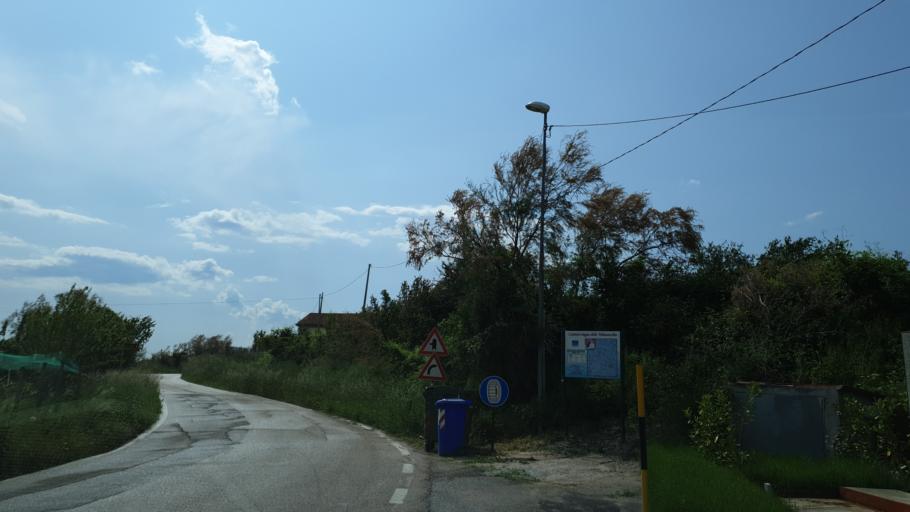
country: IT
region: Emilia-Romagna
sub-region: Provincia di Rimini
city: Sant'Agata Feltria
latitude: 43.9033
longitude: 12.2274
